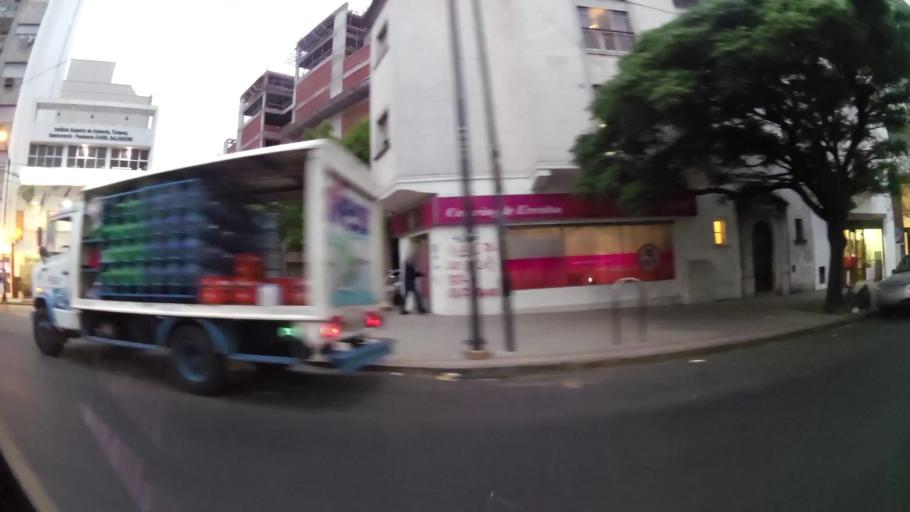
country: AR
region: Buenos Aires
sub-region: Partido de La Plata
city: La Plata
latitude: -34.9092
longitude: -57.9553
